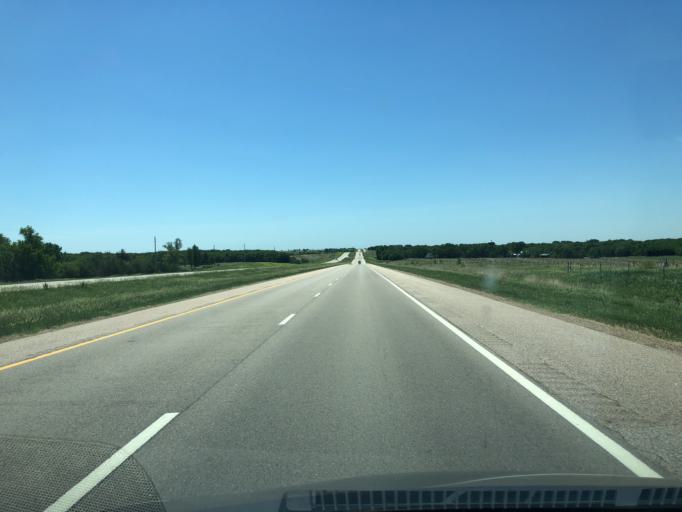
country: US
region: Kansas
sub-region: Republic County
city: Belleville
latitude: 39.9653
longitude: -97.6135
